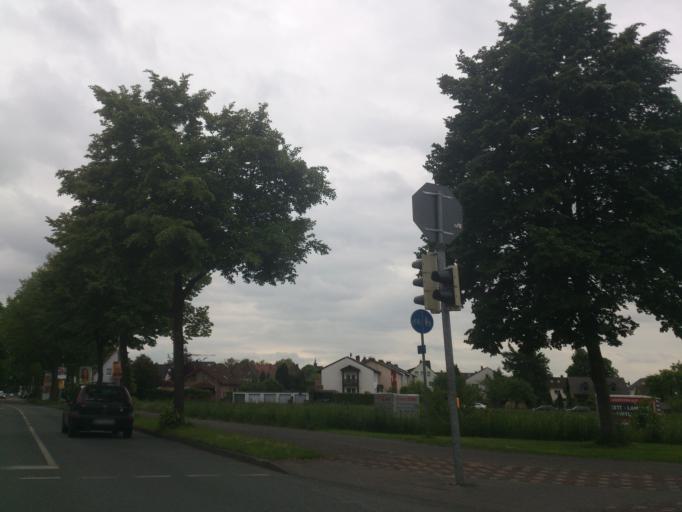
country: DE
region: North Rhine-Westphalia
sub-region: Regierungsbezirk Detmold
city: Paderborn
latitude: 51.7409
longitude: 8.7610
